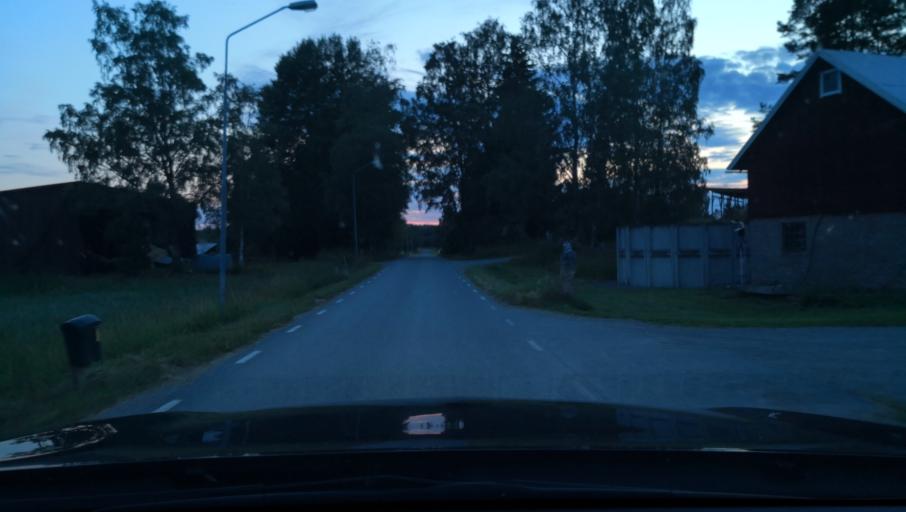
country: SE
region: Uppsala
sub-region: Osthammars Kommun
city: Bjorklinge
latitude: 60.0013
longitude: 17.3589
